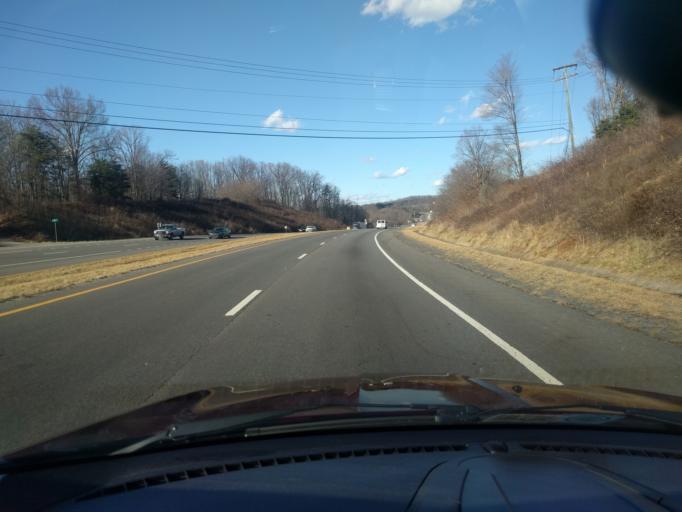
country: US
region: Virginia
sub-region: Botetourt County
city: Cloverdale
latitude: 37.3626
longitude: -79.8863
